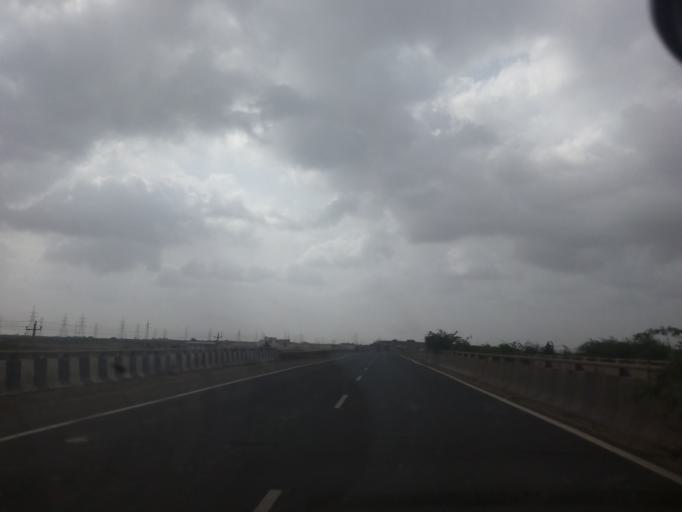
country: IN
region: Gujarat
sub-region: Rajkot
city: Morbi
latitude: 23.1333
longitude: 70.7546
